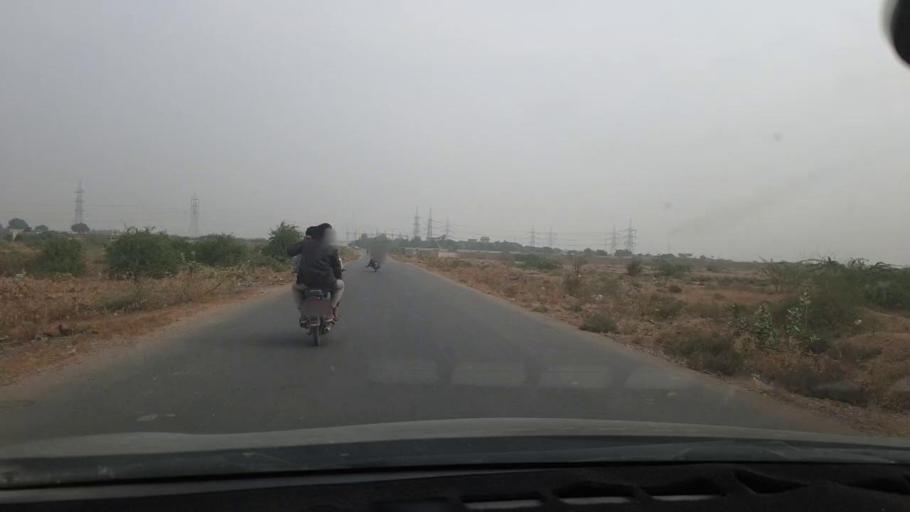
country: PK
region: Sindh
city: Malir Cantonment
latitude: 24.9129
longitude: 67.2758
